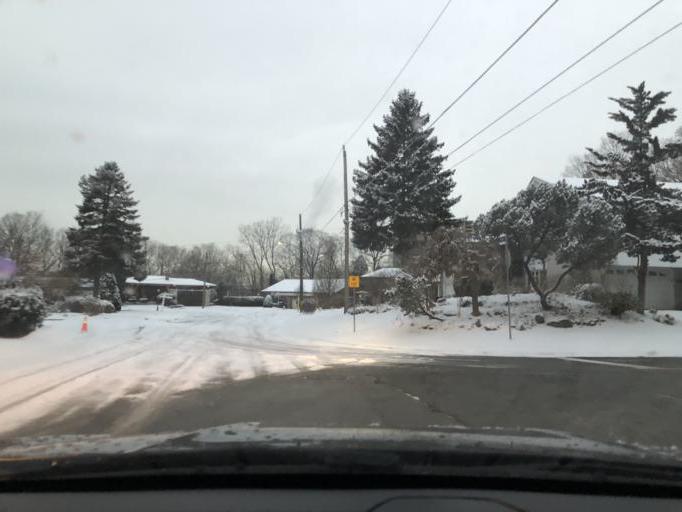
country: CA
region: Ontario
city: Toronto
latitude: 43.6964
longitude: -79.4833
